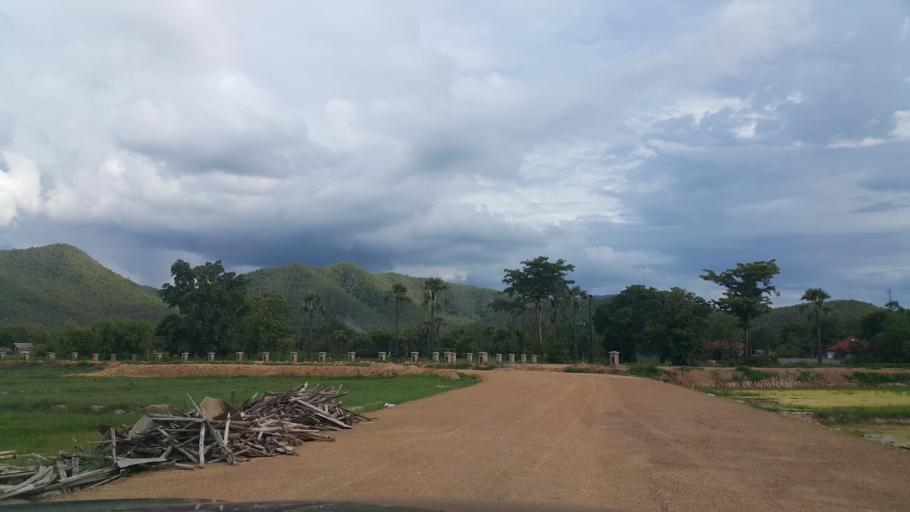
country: TH
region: Chiang Mai
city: Mae On
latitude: 18.7230
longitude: 99.2119
